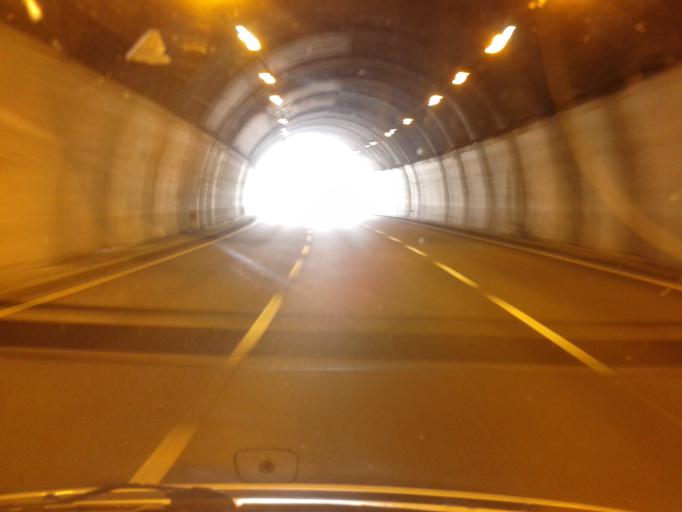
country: IT
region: Liguria
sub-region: Provincia di Genova
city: Mele
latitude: 44.4476
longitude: 8.7365
